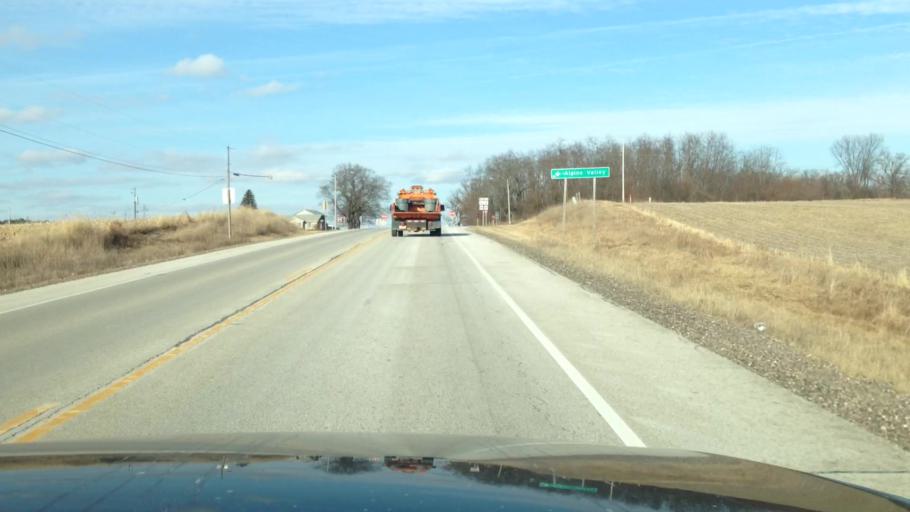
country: US
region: Wisconsin
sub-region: Walworth County
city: East Troy
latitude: 42.7443
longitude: -88.4061
